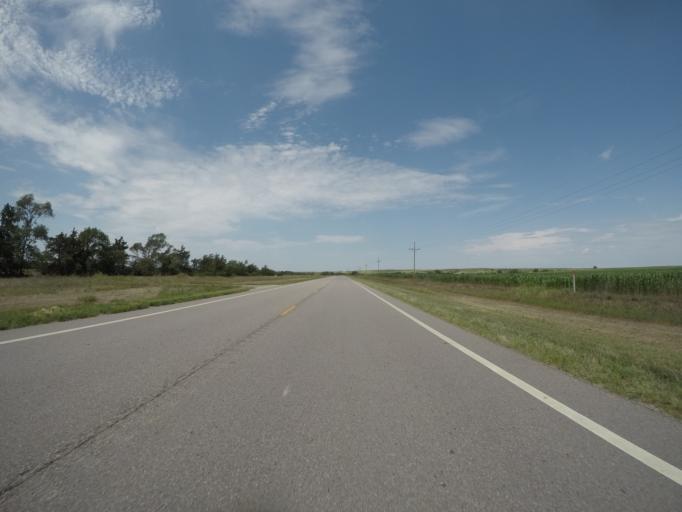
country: US
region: Kansas
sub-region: Rooks County
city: Stockton
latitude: 39.4534
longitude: -99.1224
